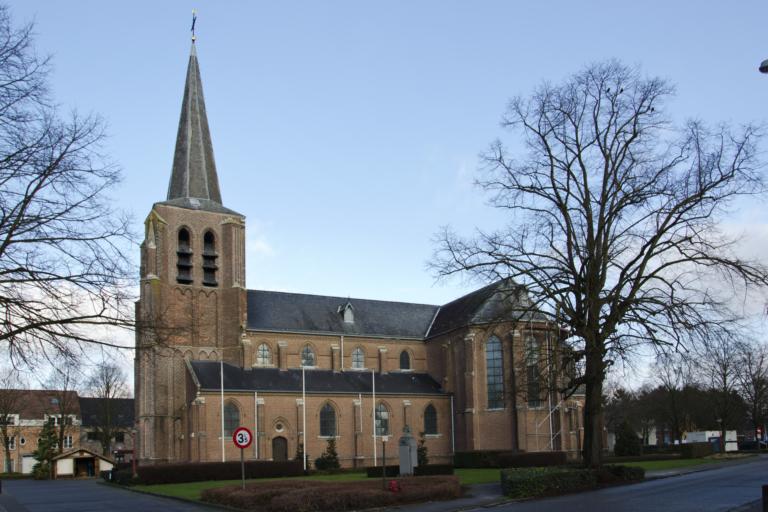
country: BE
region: Flanders
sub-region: Provincie Antwerpen
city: Olen
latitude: 51.1384
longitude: 4.9046
